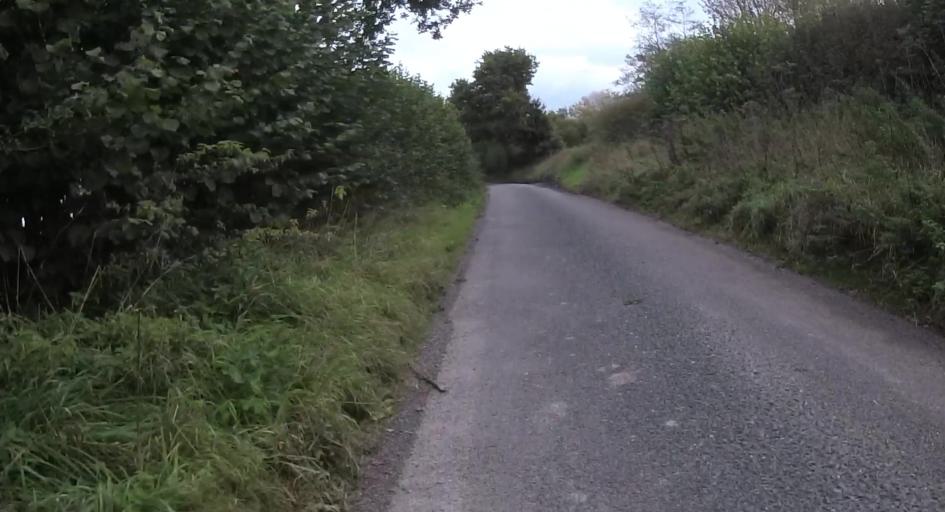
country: GB
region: England
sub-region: Hampshire
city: Alton
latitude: 51.1236
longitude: -0.9543
